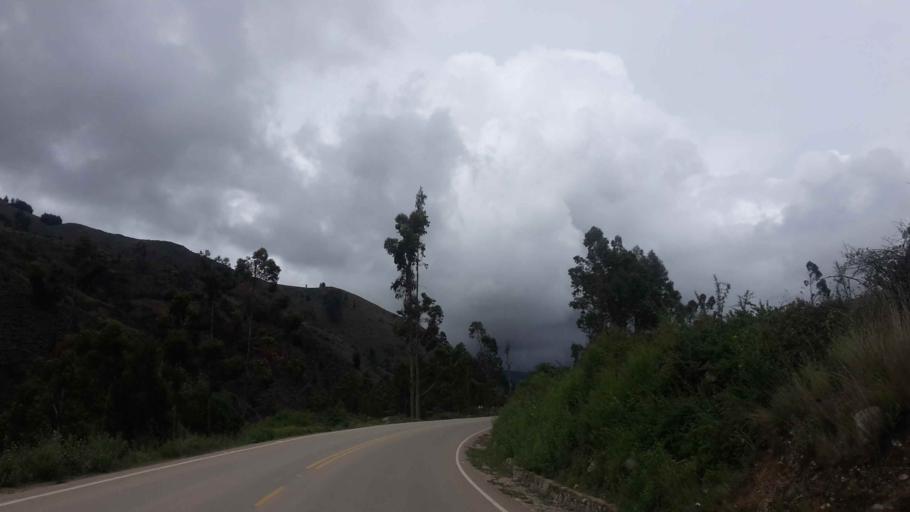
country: BO
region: Cochabamba
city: Arani
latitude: -17.4767
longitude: -65.5115
